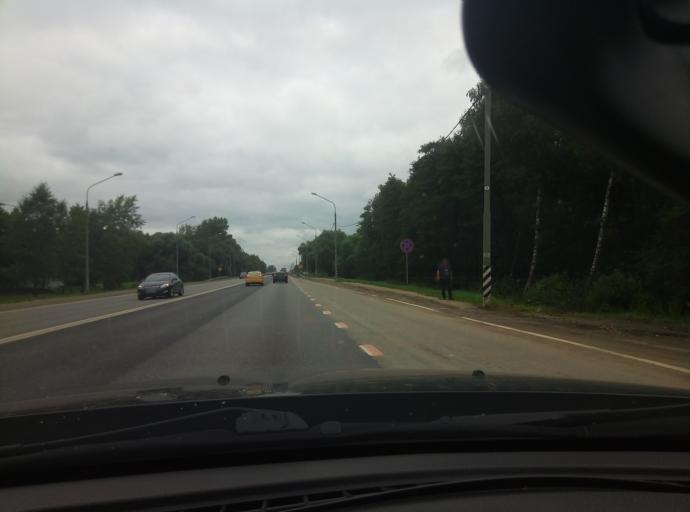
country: RU
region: Kaluga
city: Obninsk
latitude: 55.0969
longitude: 36.6376
